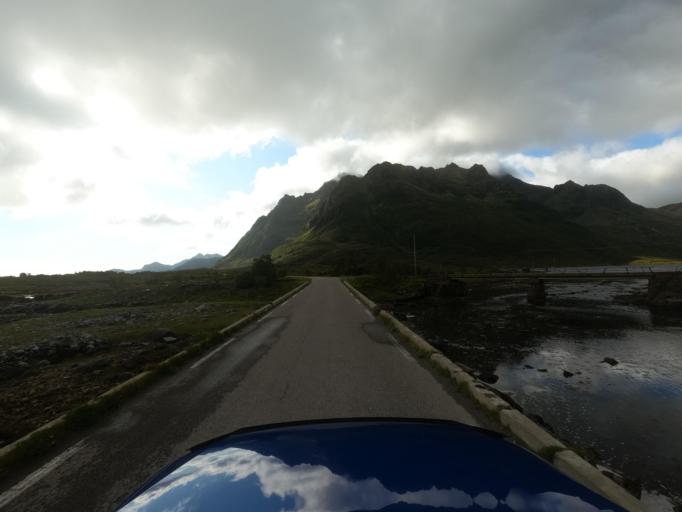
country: NO
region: Nordland
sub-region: Vestvagoy
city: Evjen
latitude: 68.1911
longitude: 13.8628
